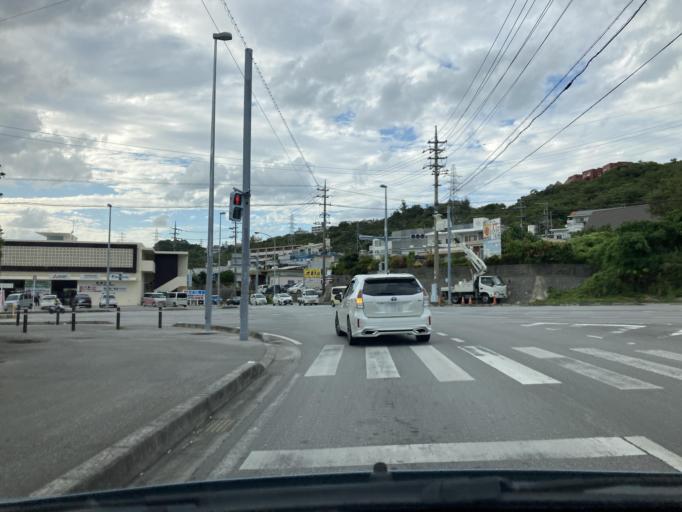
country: JP
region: Okinawa
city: Gushikawa
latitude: 26.3492
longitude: 127.8634
